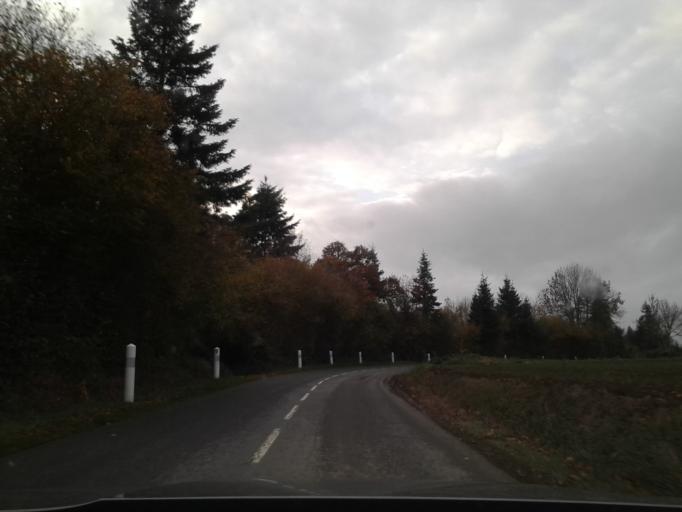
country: FR
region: Lower Normandy
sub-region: Departement du Calvados
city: Le Theil-Bocage
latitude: 48.8708
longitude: -0.6991
